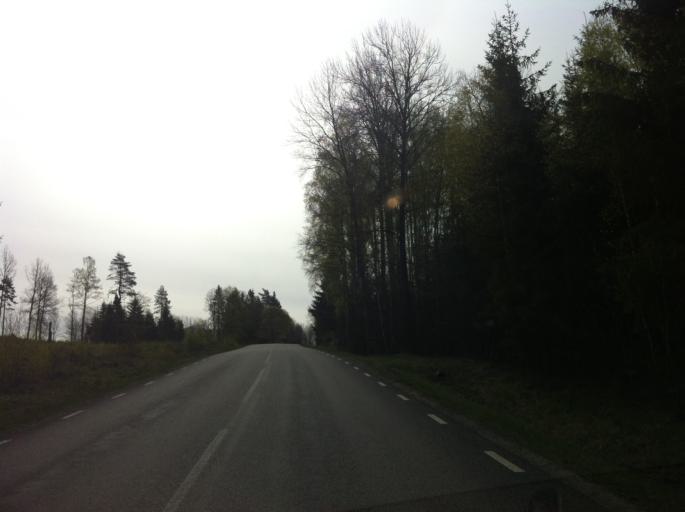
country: SE
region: Vaestra Goetaland
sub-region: Marks Kommun
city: Kinna
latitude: 57.4462
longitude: 12.7362
